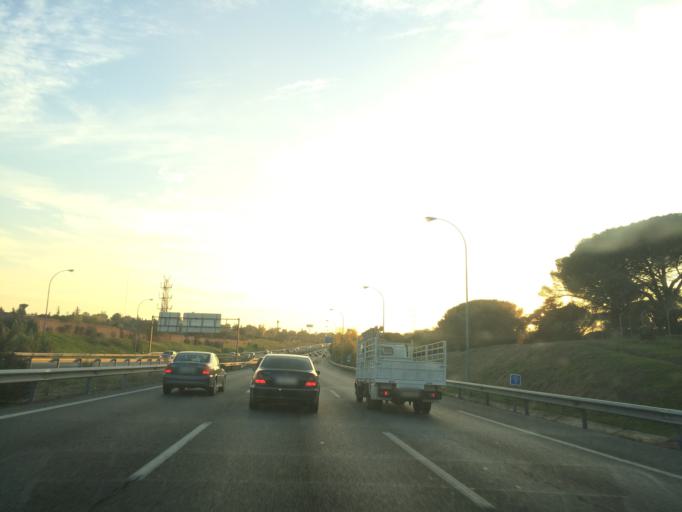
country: ES
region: Madrid
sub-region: Provincia de Madrid
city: Pozuelo de Alarcon
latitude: 40.4497
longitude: -3.8210
